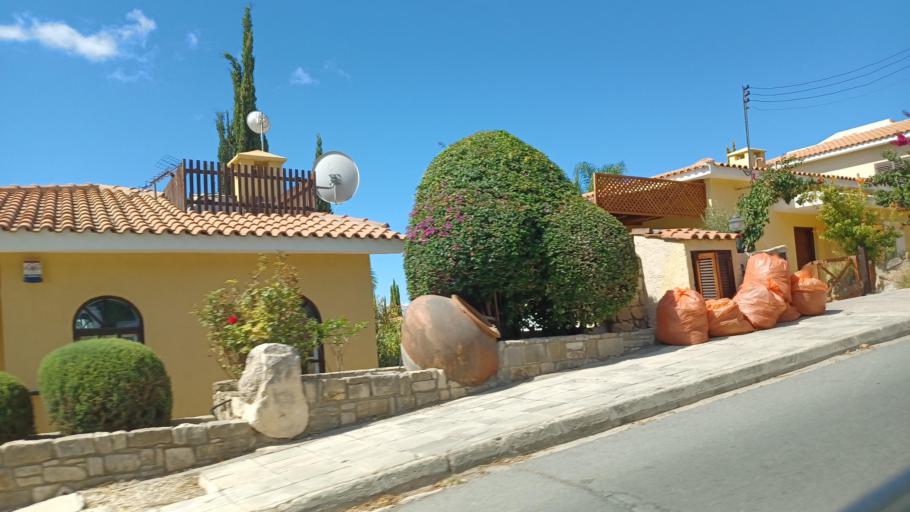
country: CY
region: Pafos
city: Tala
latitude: 34.8447
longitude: 32.4339
